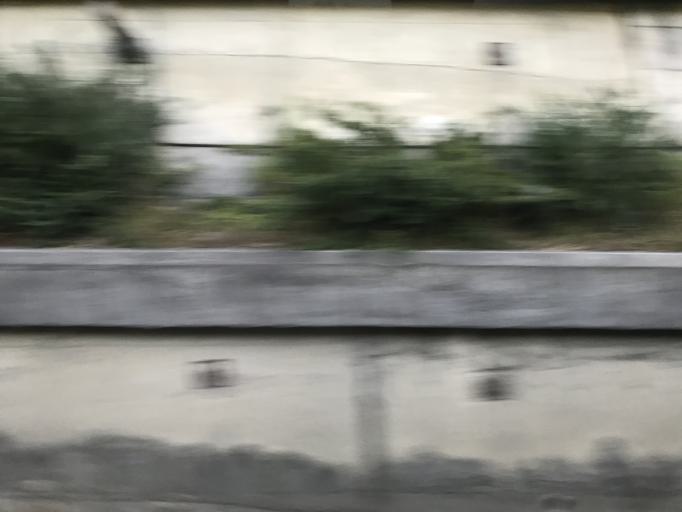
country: ES
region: Basque Country
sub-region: Provincia de Guipuzcoa
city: Isasondo
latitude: 43.0712
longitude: -2.1601
